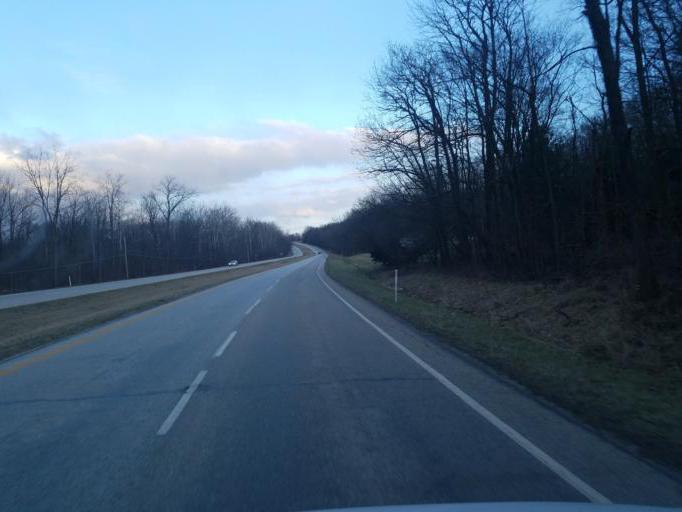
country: US
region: Indiana
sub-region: Henry County
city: Knightstown
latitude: 39.8039
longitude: -85.4957
